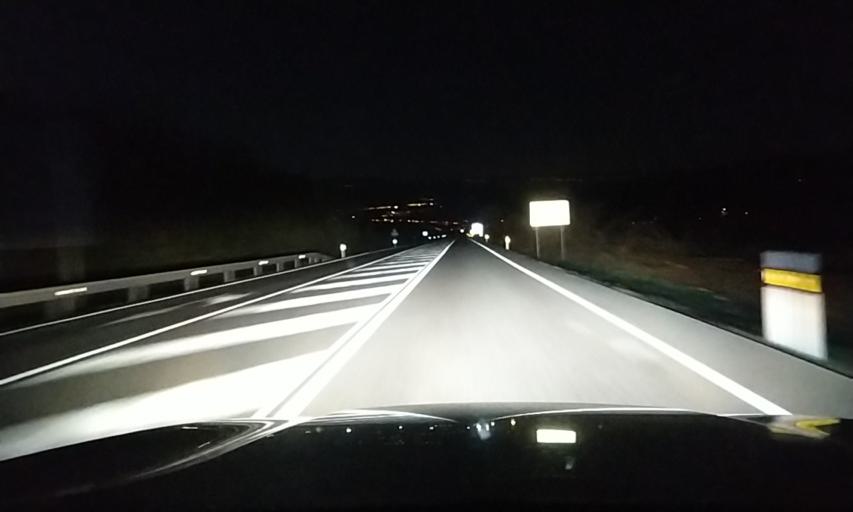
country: ES
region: Galicia
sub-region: Provincia de Ourense
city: Cualedro
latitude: 41.9796
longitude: -7.5247
